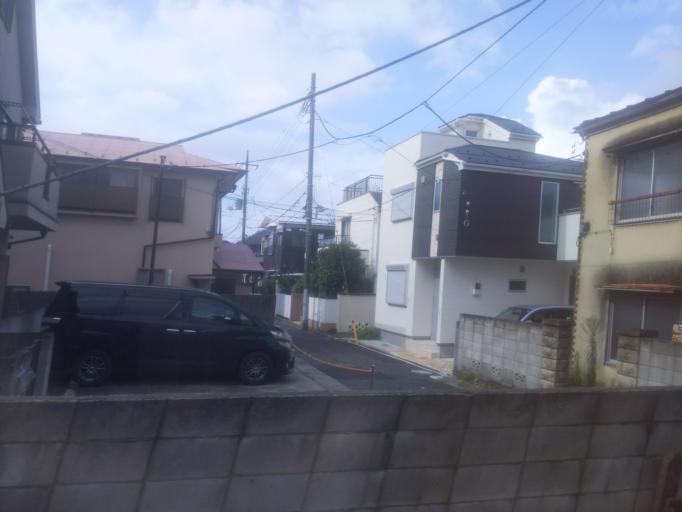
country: JP
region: Tokyo
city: Tokyo
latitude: 35.7213
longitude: 139.6480
